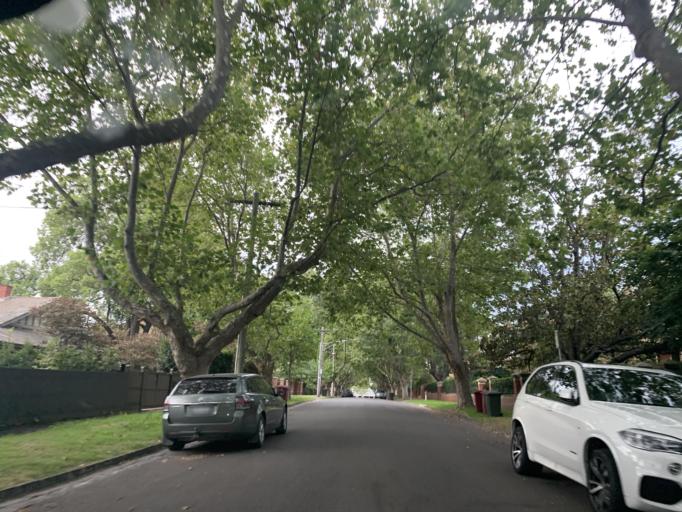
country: AU
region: Victoria
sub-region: Stonnington
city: Malvern East
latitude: -37.8734
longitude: 145.0441
